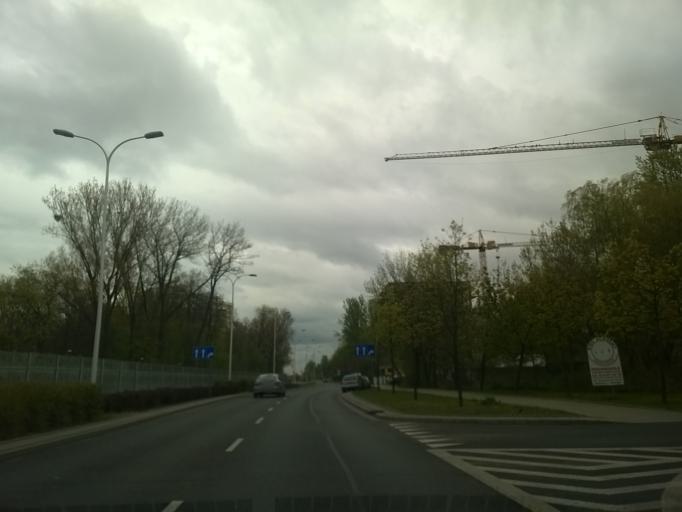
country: PL
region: Masovian Voivodeship
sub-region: Warszawa
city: Ursynow
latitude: 52.1709
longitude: 21.0626
